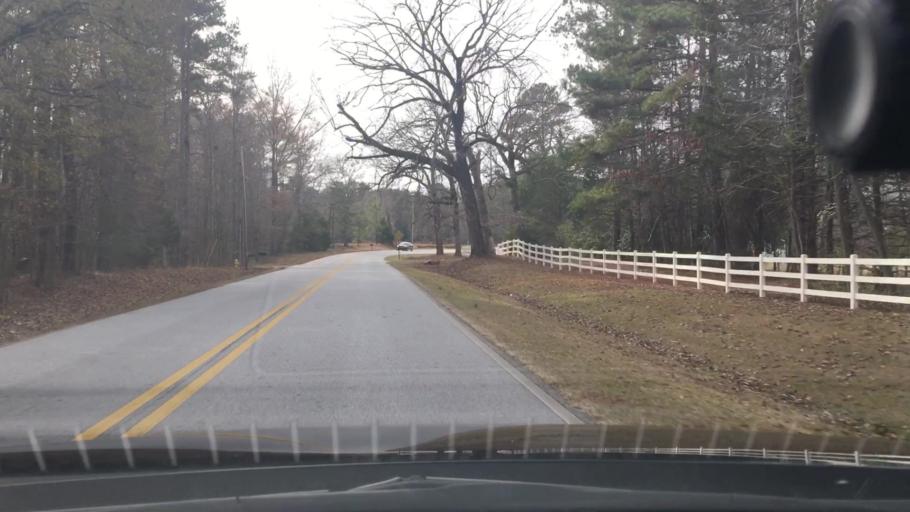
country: US
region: Georgia
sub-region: Spalding County
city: Experiment
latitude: 33.2786
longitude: -84.4163
